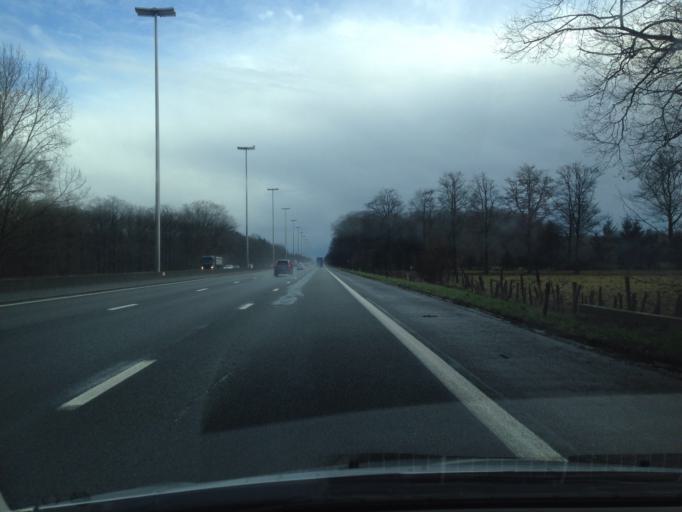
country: BE
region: Flanders
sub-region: Provincie West-Vlaanderen
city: Beernem
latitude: 51.1095
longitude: 3.3632
